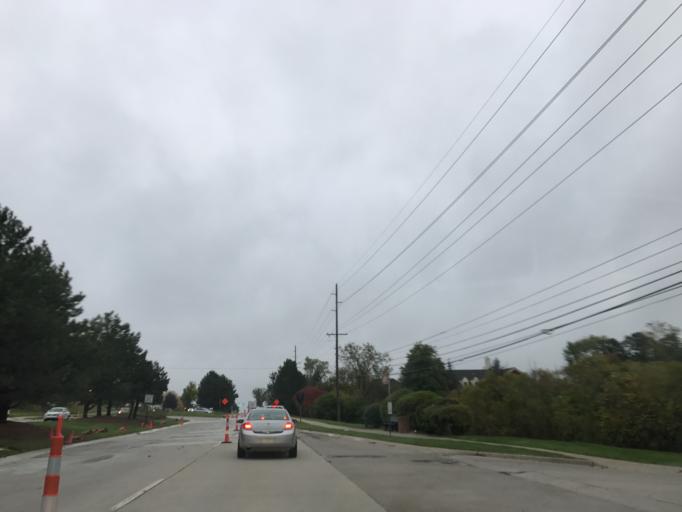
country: US
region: Michigan
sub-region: Oakland County
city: Farmington Hills
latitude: 42.4974
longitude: -83.4238
